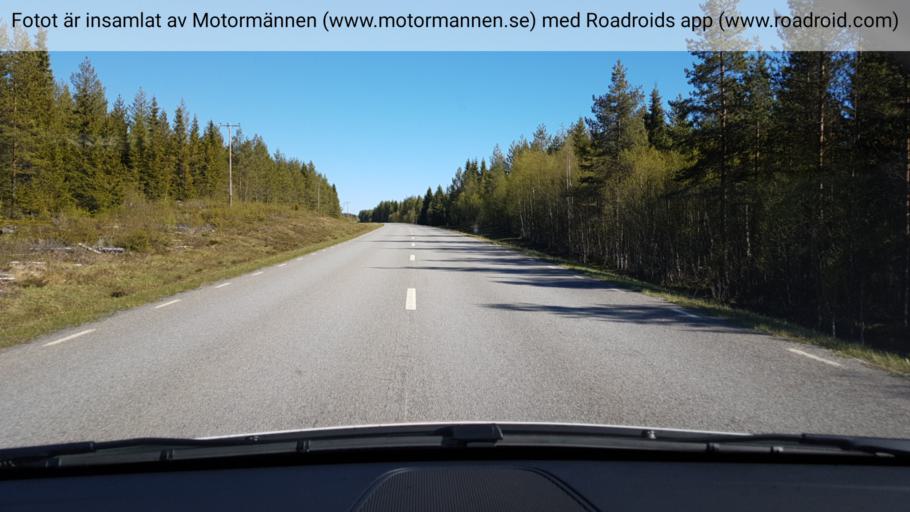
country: SE
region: Jaemtland
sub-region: Stroemsunds Kommun
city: Stroemsund
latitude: 64.2840
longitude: 15.3547
